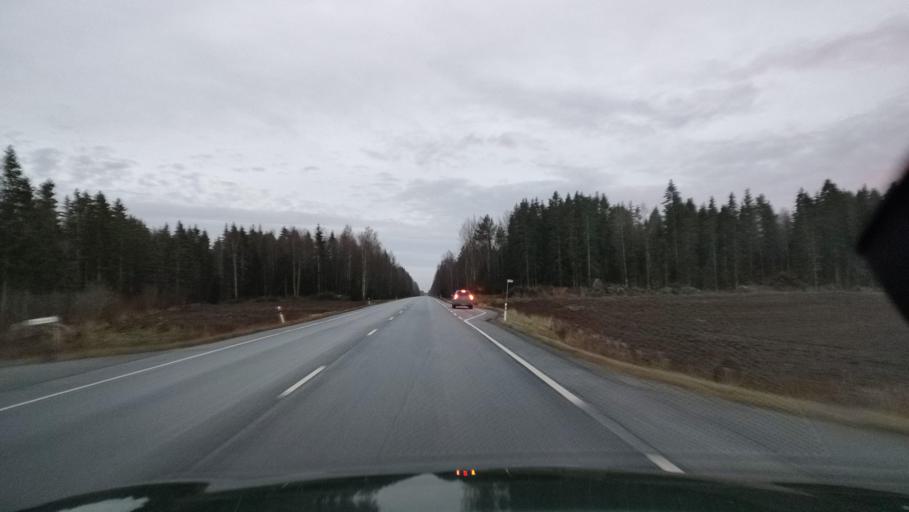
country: FI
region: Ostrobothnia
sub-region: Vaasa
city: Ristinummi
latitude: 63.0062
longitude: 21.7630
